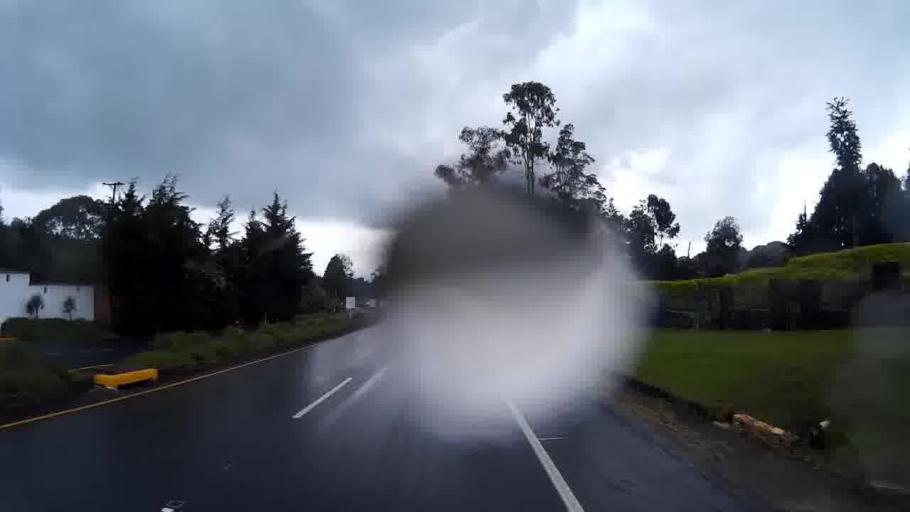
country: CO
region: Quindio
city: Circasia
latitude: 4.6334
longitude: -75.6155
